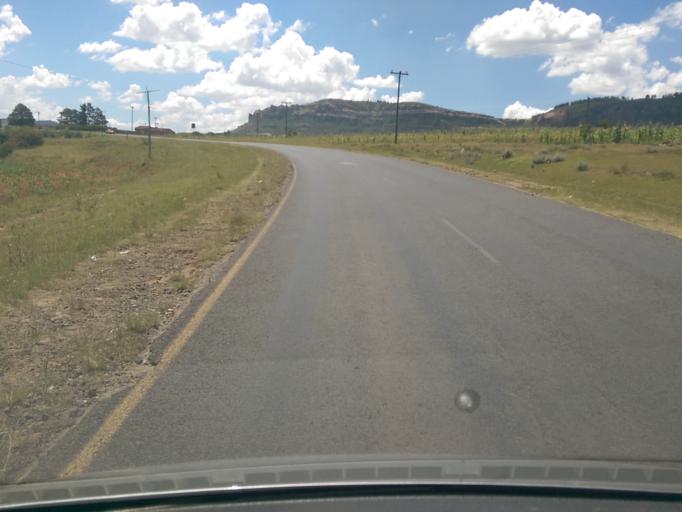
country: LS
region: Maseru
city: Nako
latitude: -29.4265
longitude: 27.6761
